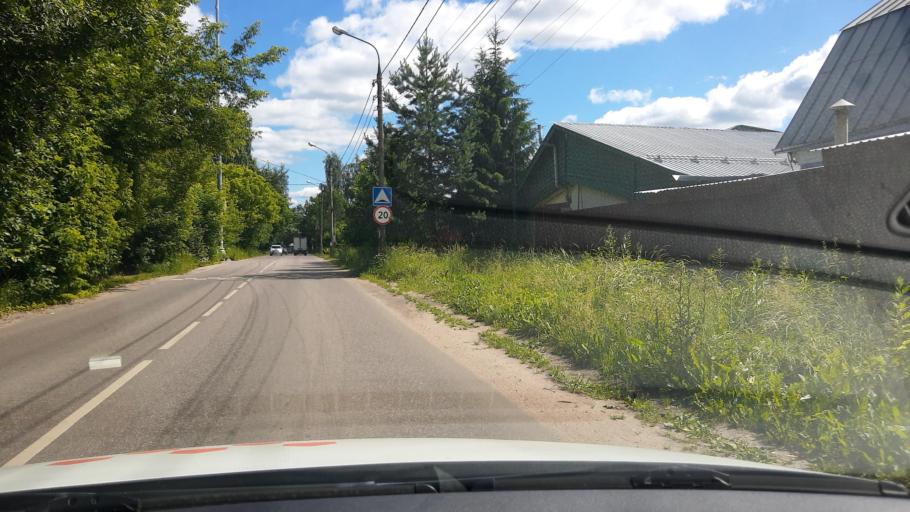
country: RU
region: Moskovskaya
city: Noginsk
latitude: 55.8747
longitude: 38.4381
